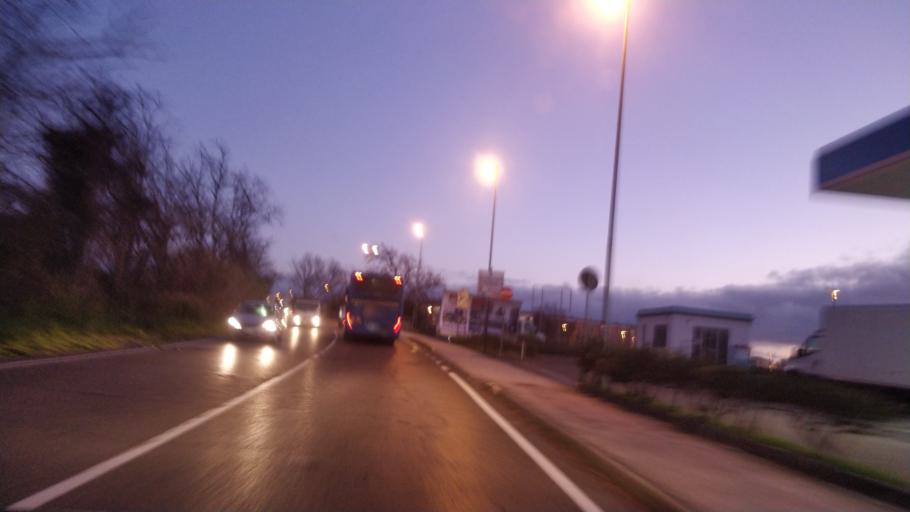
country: IT
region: Tuscany
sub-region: Provincia di Livorno
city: Cecina
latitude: 43.3165
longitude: 10.5135
